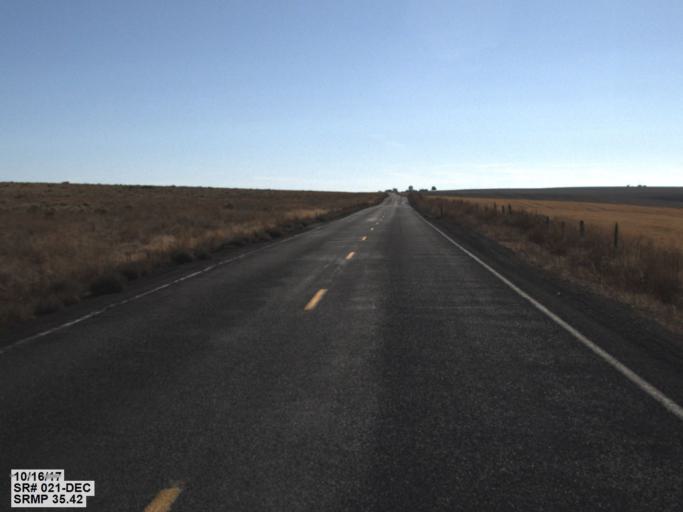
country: US
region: Washington
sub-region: Adams County
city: Ritzville
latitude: 47.0632
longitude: -118.6630
